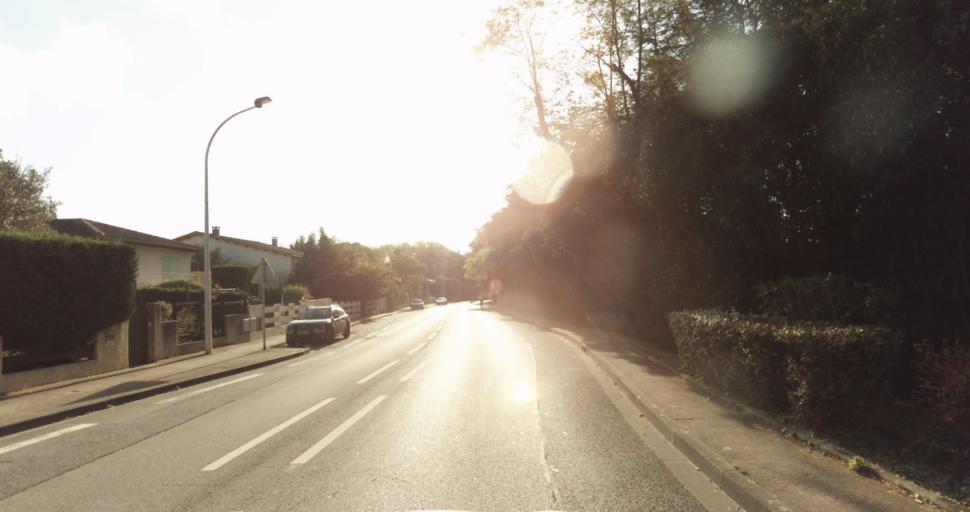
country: FR
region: Midi-Pyrenees
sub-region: Departement de la Haute-Garonne
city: Ramonville-Saint-Agne
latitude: 43.5411
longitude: 1.4616
